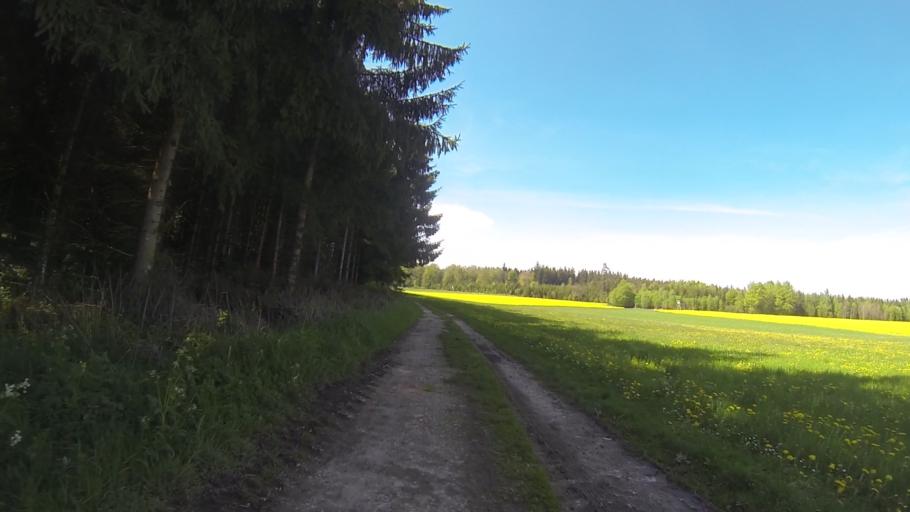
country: DE
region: Baden-Wuerttemberg
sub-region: Regierungsbezirk Stuttgart
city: Bartholoma
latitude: 48.7646
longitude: 10.0213
